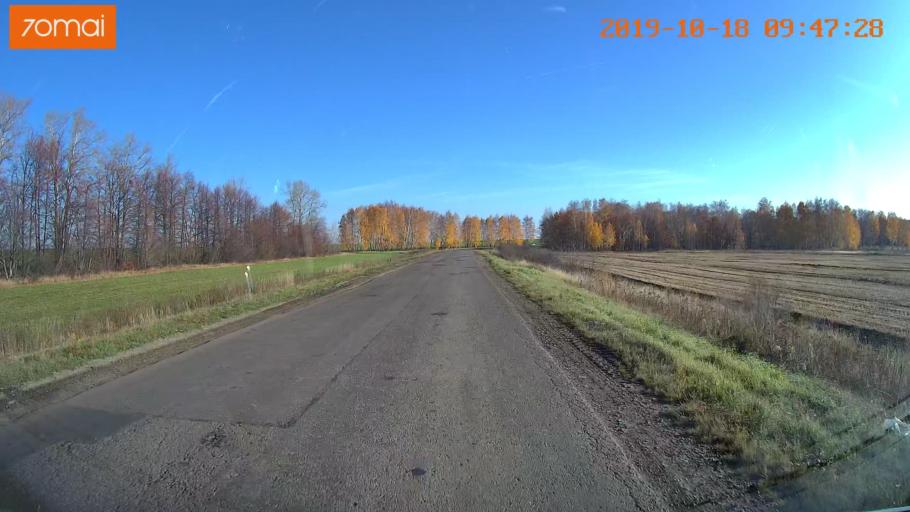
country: RU
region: Tula
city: Kazachka
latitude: 53.3191
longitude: 38.2319
